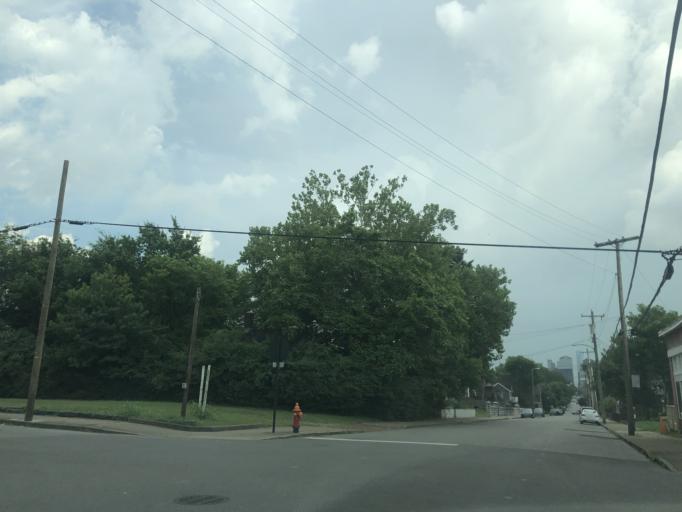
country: US
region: Tennessee
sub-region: Davidson County
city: Nashville
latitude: 36.1841
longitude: -86.7938
